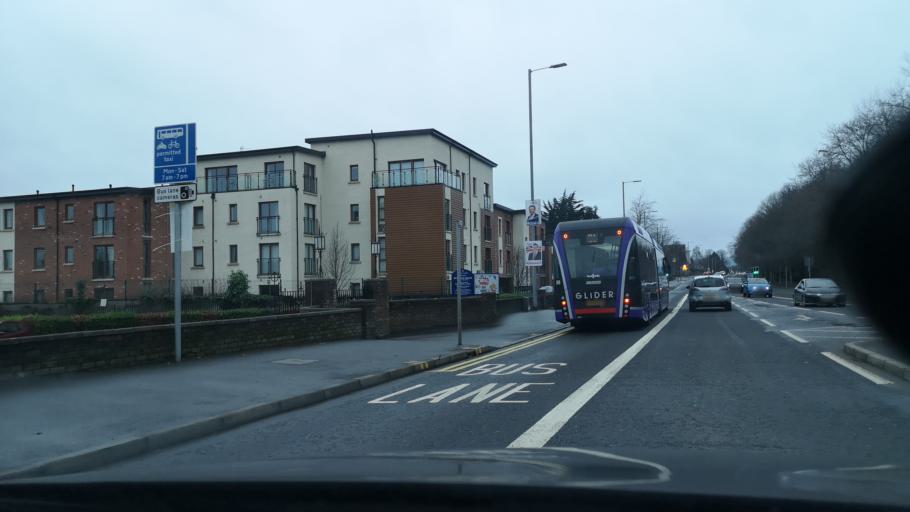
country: GB
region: Northern Ireland
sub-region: Castlereagh District
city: Dundonald
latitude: 54.5948
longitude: -5.8343
